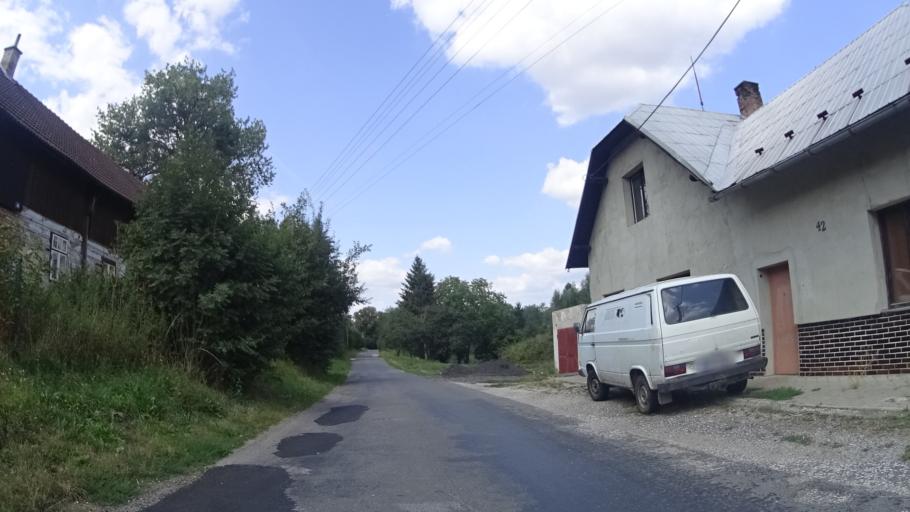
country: CZ
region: Kralovehradecky
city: Kopidlno
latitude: 50.3894
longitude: 15.2928
